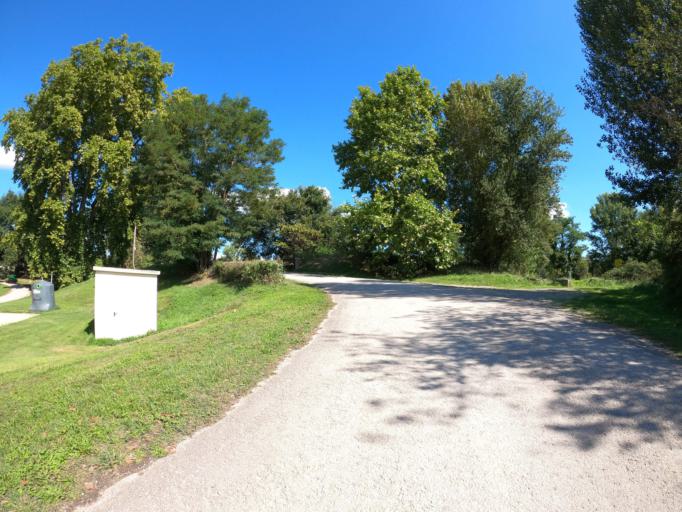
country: FR
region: Midi-Pyrenees
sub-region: Departement du Tarn-et-Garonne
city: Valence
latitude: 44.1054
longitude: 0.8859
